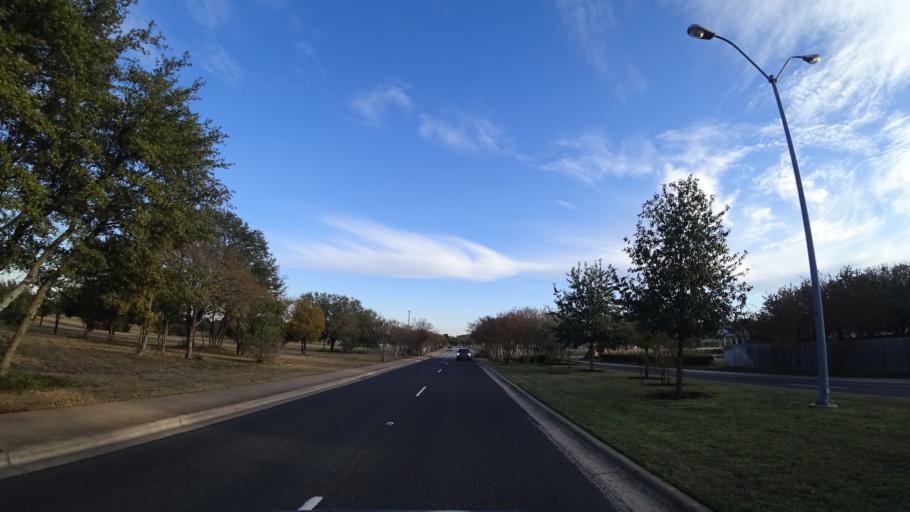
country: US
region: Texas
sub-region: Williamson County
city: Brushy Creek
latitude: 30.4974
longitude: -97.7388
